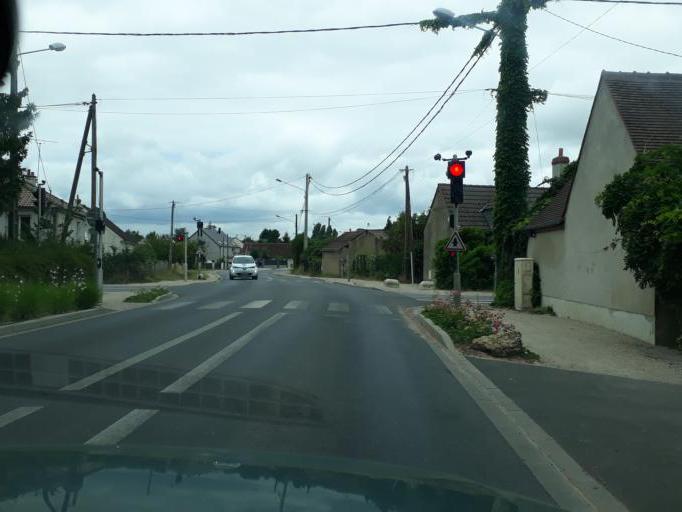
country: FR
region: Centre
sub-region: Departement du Loiret
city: Sandillon
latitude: 47.8502
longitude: 2.0224
